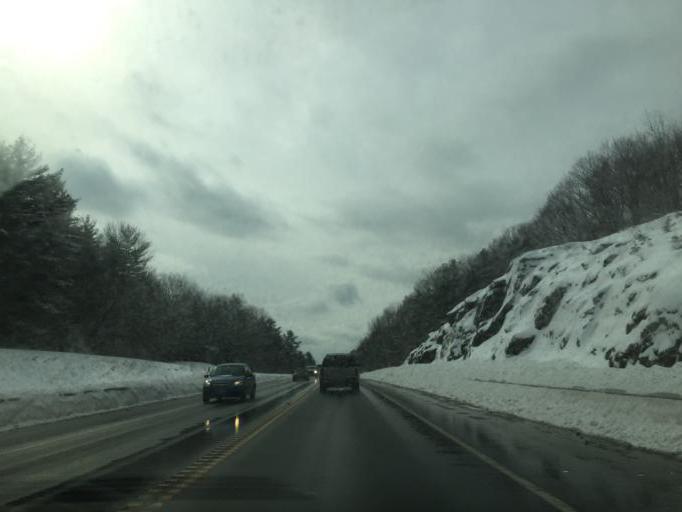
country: US
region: New Hampshire
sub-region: Carroll County
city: Sanbornville
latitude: 43.5168
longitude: -71.0284
